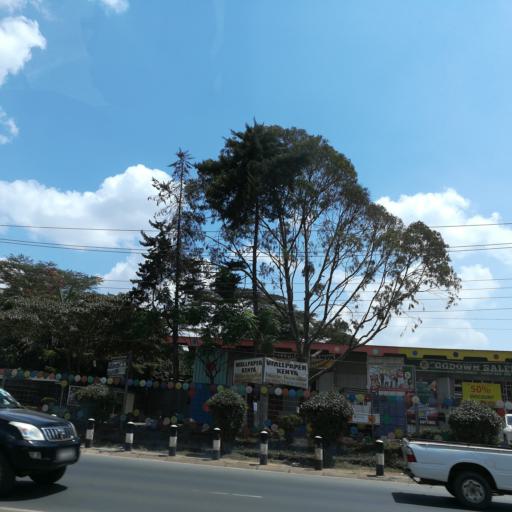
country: KE
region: Nairobi Area
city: Nairobi
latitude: -1.3104
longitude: 36.8177
